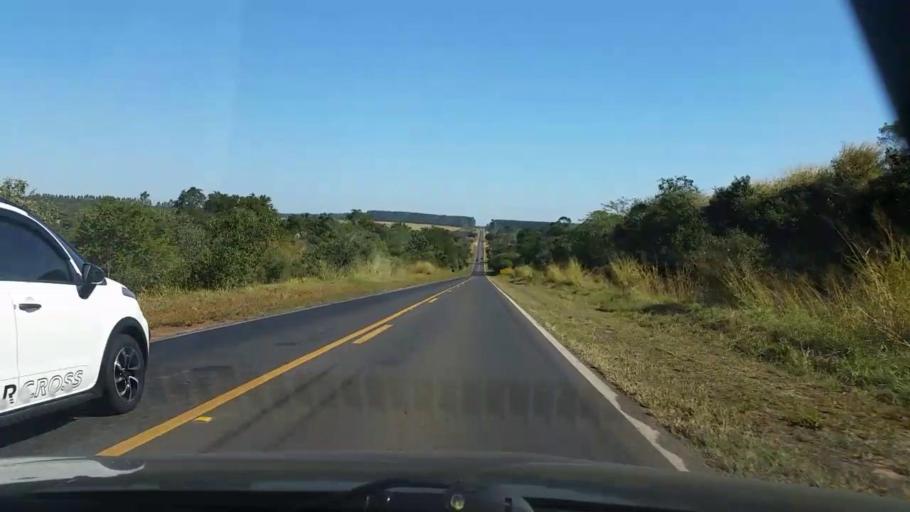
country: BR
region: Sao Paulo
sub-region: Avare
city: Avare
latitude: -22.9092
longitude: -48.7724
